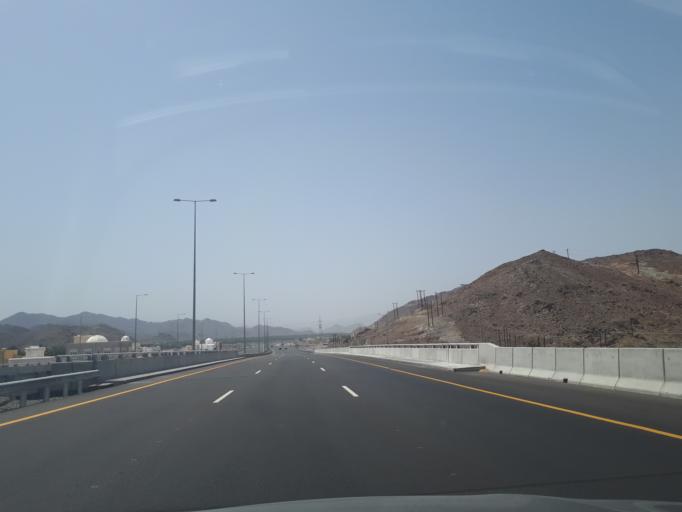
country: OM
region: Muhafazat ad Dakhiliyah
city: Bidbid
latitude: 23.3913
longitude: 58.1004
